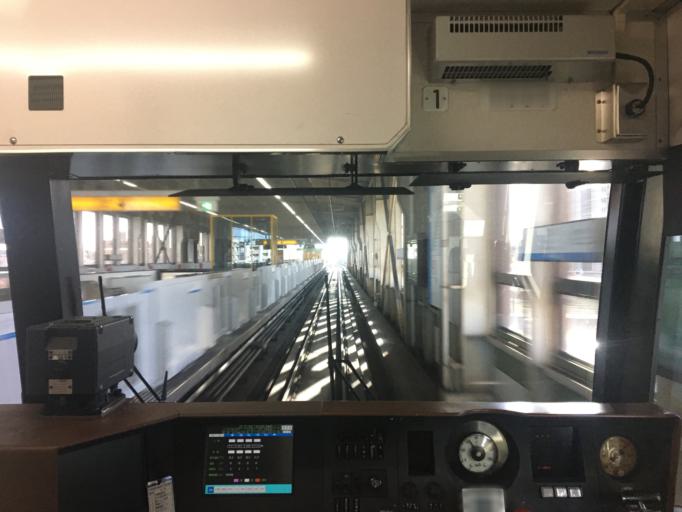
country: JP
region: Miyagi
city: Sendai
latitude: 38.2144
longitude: 140.8707
